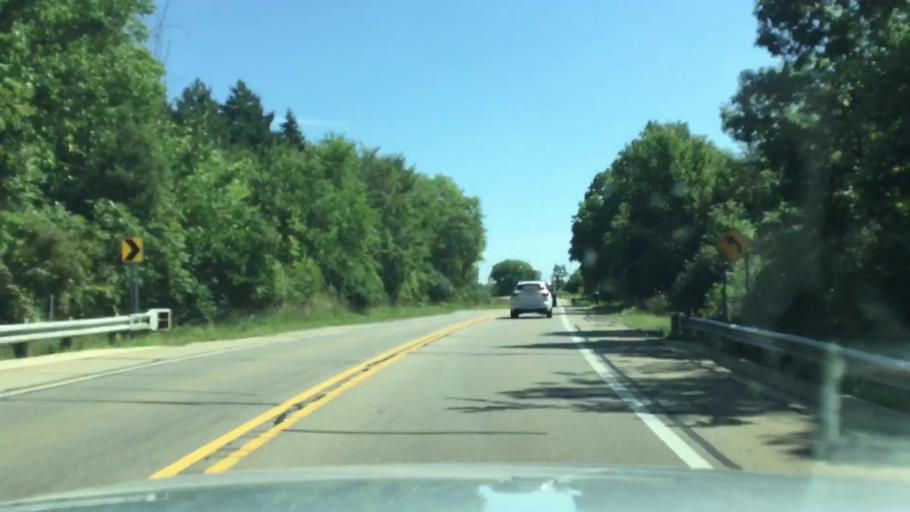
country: US
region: Michigan
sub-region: Washtenaw County
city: Manchester
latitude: 42.0717
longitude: -84.0937
